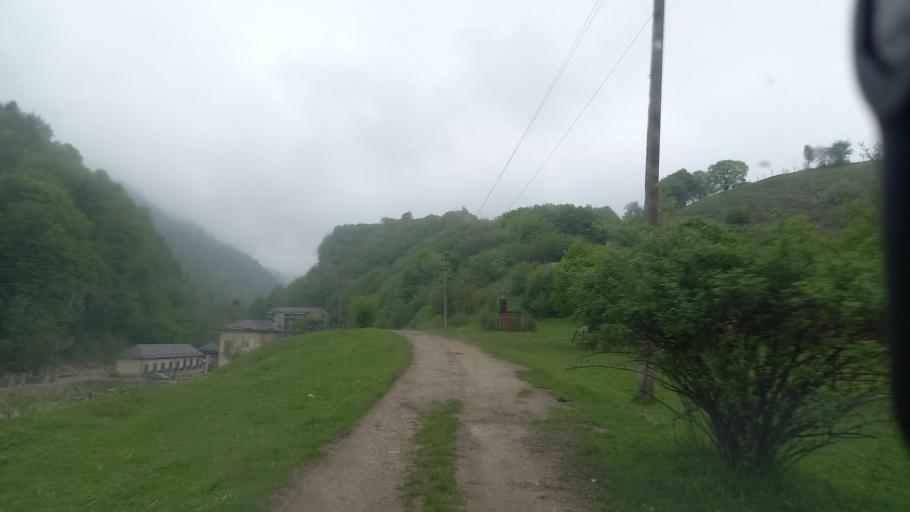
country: RU
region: Kabardino-Balkariya
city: Babugent
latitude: 43.2501
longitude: 43.5304
